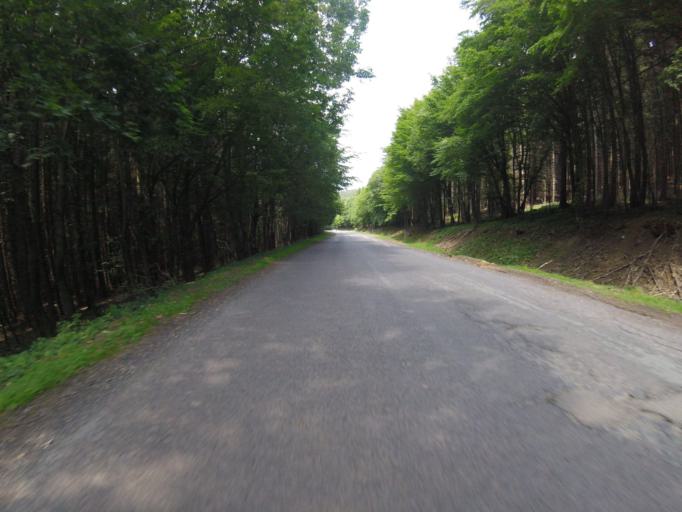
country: HU
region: Nograd
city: Batonyterenye
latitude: 47.8958
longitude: 19.8585
